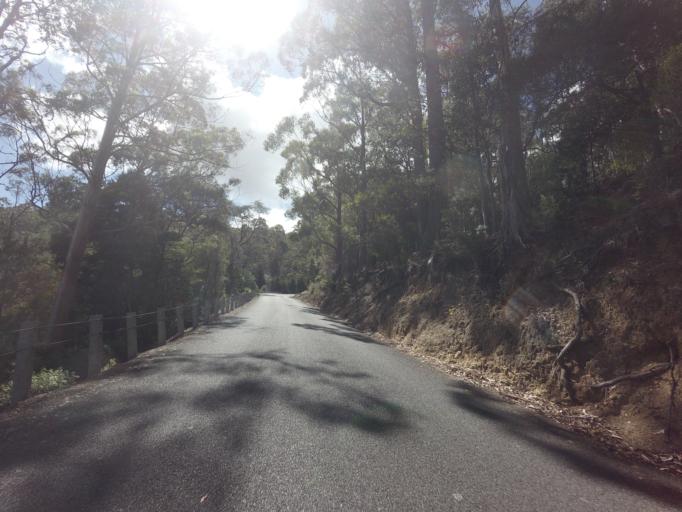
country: AU
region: Tasmania
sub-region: Break O'Day
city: St Helens
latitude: -41.6362
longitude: 148.2435
